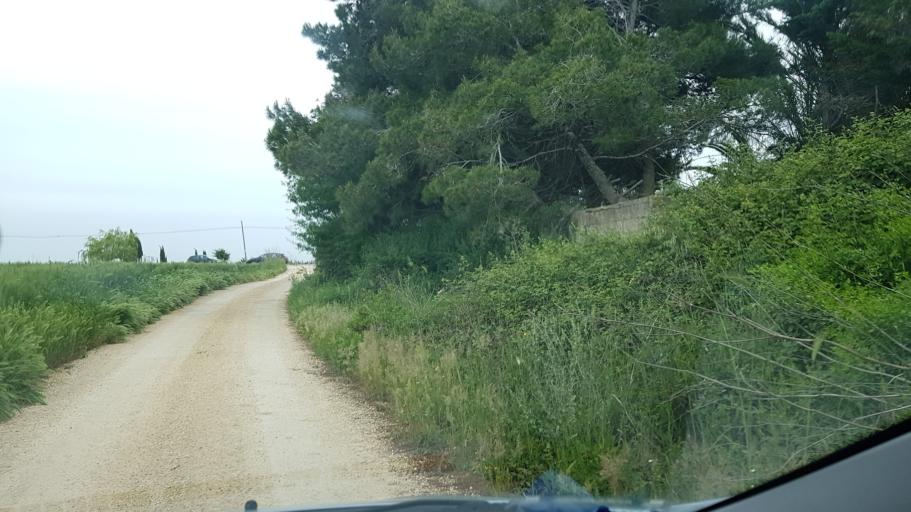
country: IT
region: Apulia
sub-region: Provincia di Brindisi
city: Brindisi
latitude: 40.6479
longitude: 17.8833
